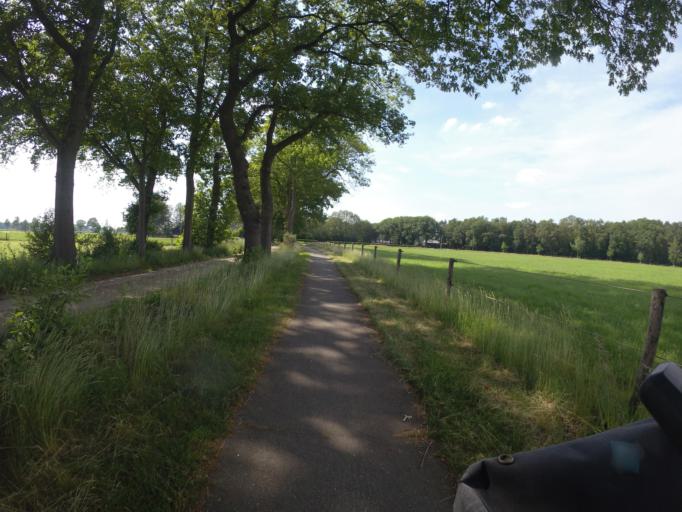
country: NL
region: Overijssel
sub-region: Gemeente Raalte
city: Raalte
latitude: 52.4375
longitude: 6.3069
